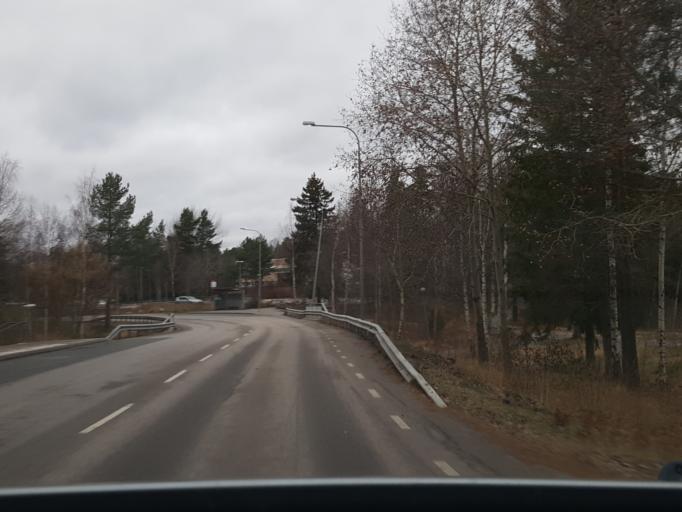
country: SE
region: Stockholm
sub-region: Nacka Kommun
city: Boo
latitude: 59.3315
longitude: 18.2719
